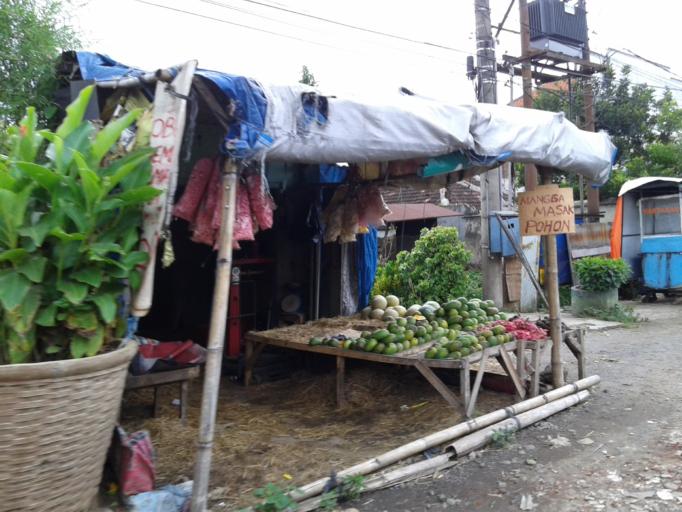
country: ID
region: East Java
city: Lawang
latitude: -7.8548
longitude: 112.6913
